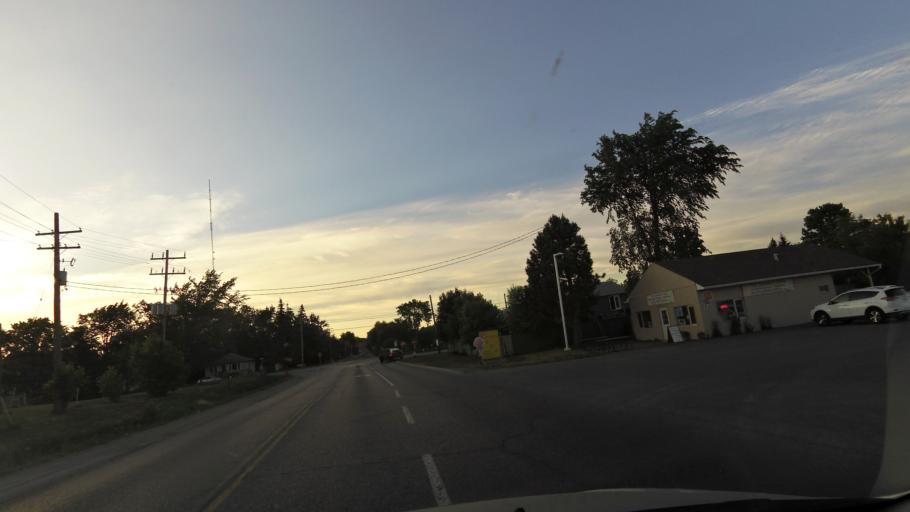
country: CA
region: Ontario
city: Peterborough
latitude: 44.3215
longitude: -78.2929
